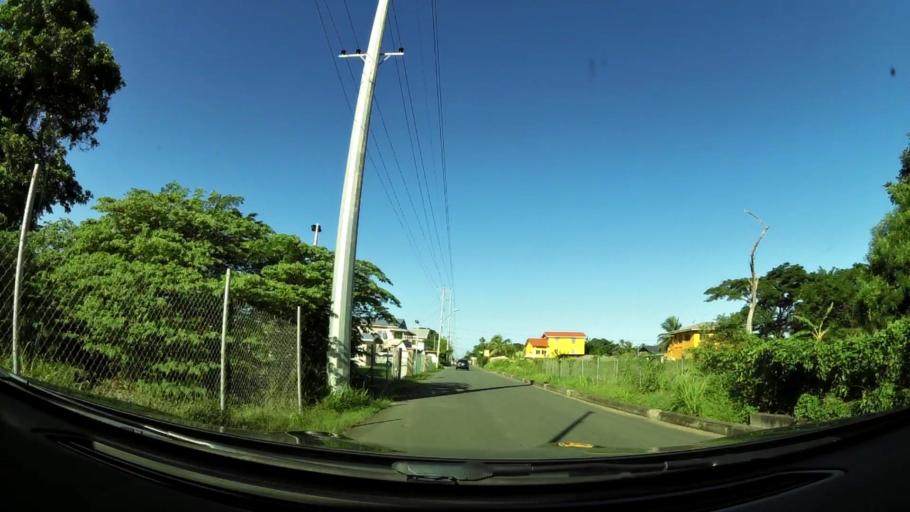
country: TT
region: Tobago
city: Scarborough
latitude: 11.1521
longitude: -60.8145
